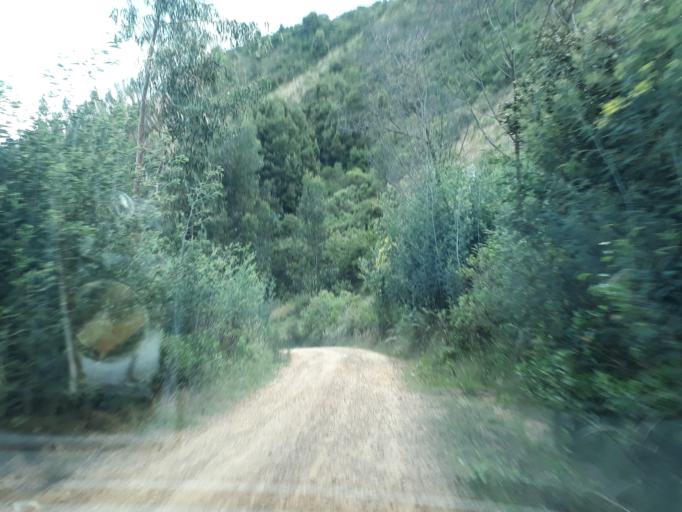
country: CO
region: Boyaca
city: Santa Rosa de Viterbo
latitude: 5.8634
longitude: -72.9680
